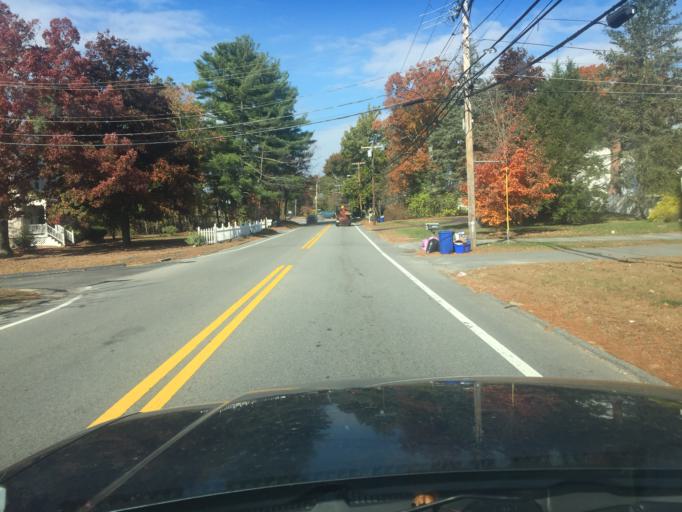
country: US
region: Massachusetts
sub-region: Worcester County
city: Milford
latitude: 42.1058
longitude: -71.5051
